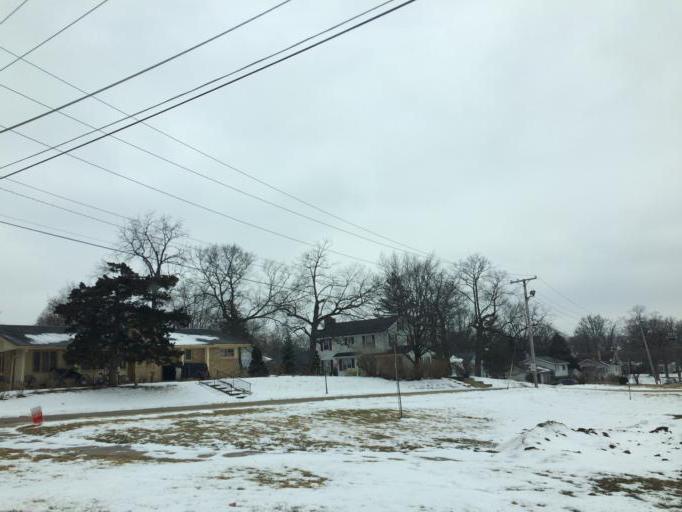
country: US
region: Illinois
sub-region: McHenry County
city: Harvard
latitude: 42.4277
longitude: -88.6087
